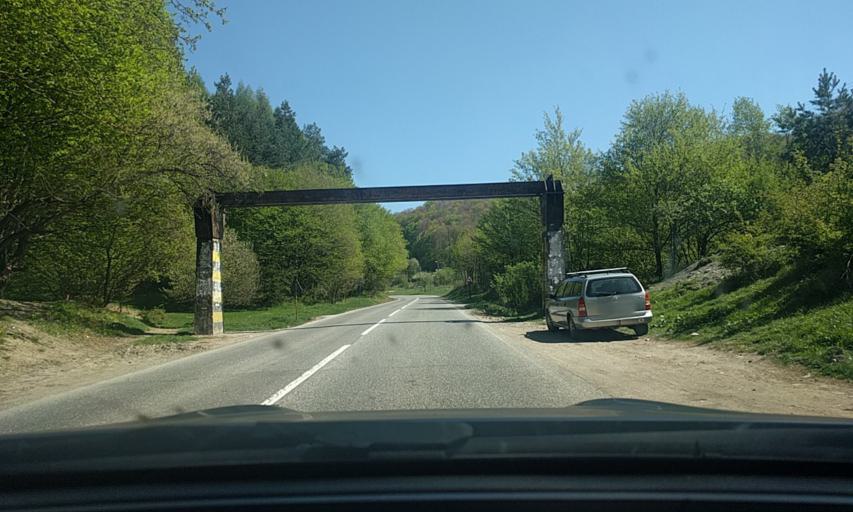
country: RO
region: Brasov
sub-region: Comuna Vama Buzaului
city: Acris
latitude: 45.6786
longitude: 25.9392
